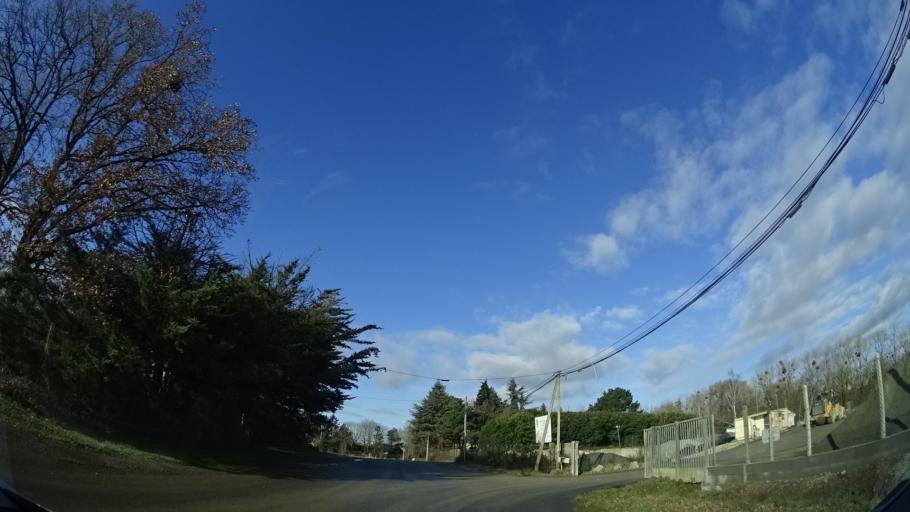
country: FR
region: Brittany
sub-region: Departement d'Ille-et-Vilaine
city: Chantepie
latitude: 48.0808
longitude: -1.6020
